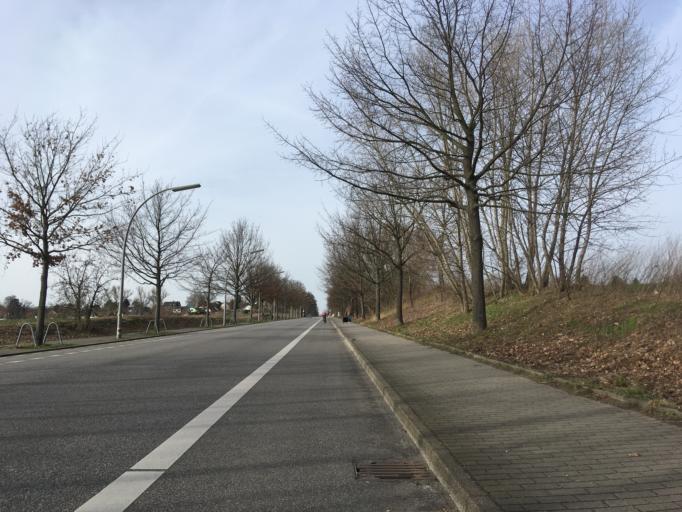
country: DE
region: Berlin
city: Lubars
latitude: 52.6098
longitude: 13.3607
